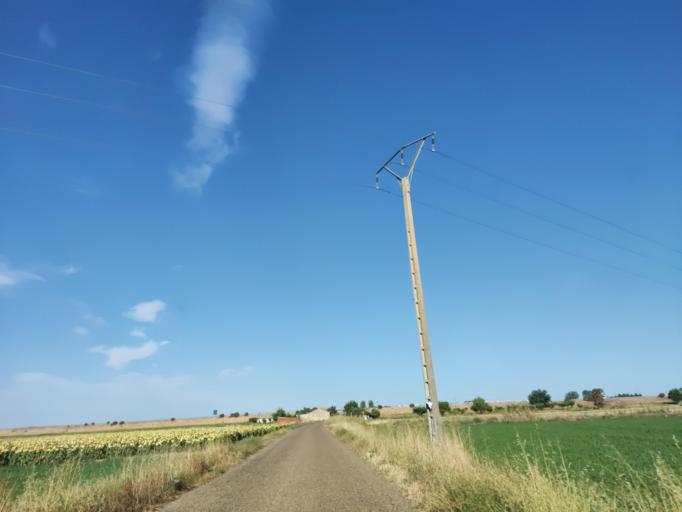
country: ES
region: Castille and Leon
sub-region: Provincia de Zamora
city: Zamora
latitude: 41.4993
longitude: -5.7225
